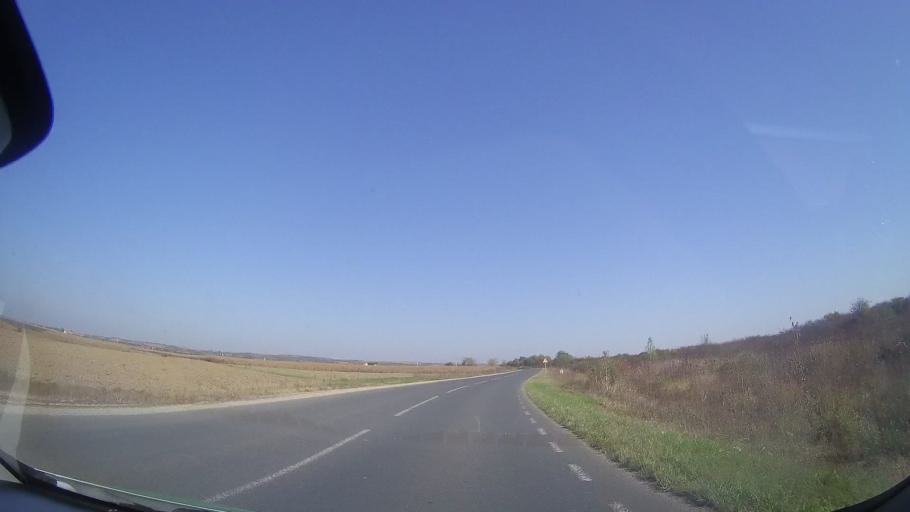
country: RO
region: Timis
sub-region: Comuna Balint
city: Balint
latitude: 45.7910
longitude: 21.8576
